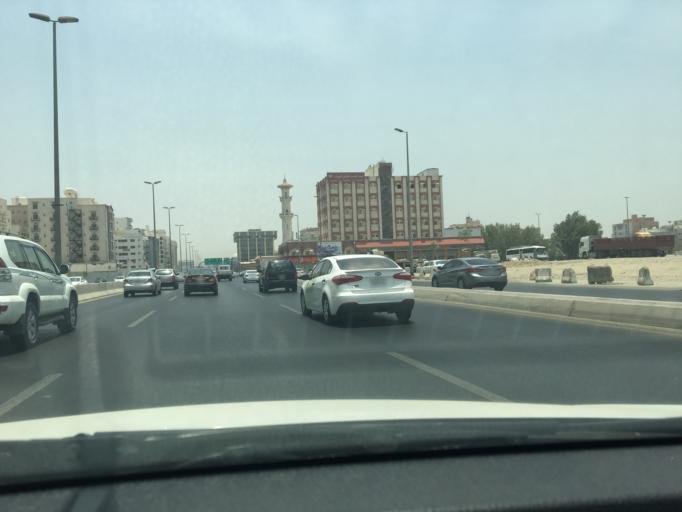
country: SA
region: Makkah
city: Jeddah
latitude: 21.5234
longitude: 39.1926
